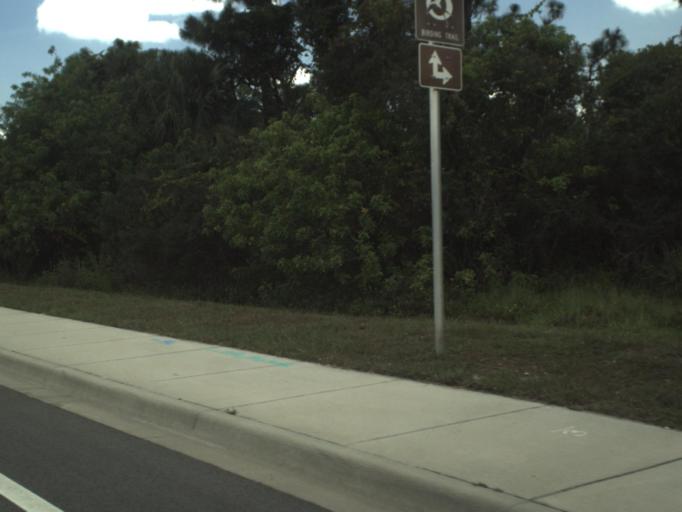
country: US
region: Florida
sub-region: Martin County
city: Palm City
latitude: 27.1575
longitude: -80.2467
